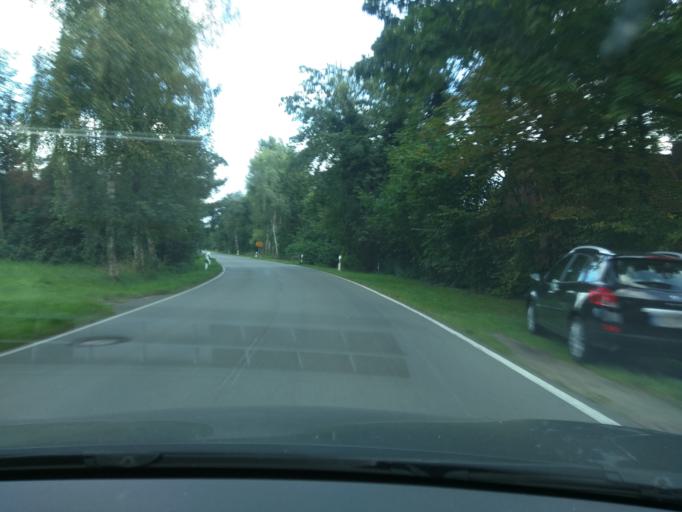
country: DE
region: Lower Saxony
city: Tespe
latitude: 53.3904
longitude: 10.4282
